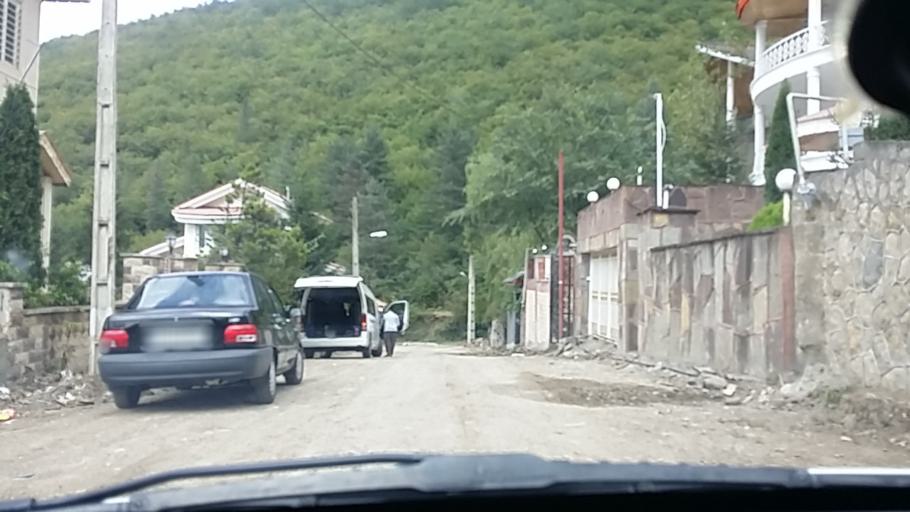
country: IR
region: Mazandaran
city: `Abbasabad
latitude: 36.4904
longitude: 51.1668
